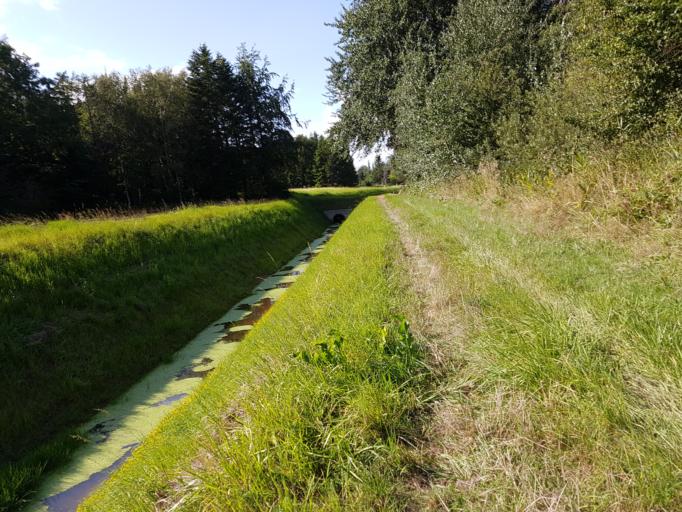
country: DK
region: Zealand
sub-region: Guldborgsund Kommune
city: Nykobing Falster
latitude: 54.6019
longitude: 11.9481
